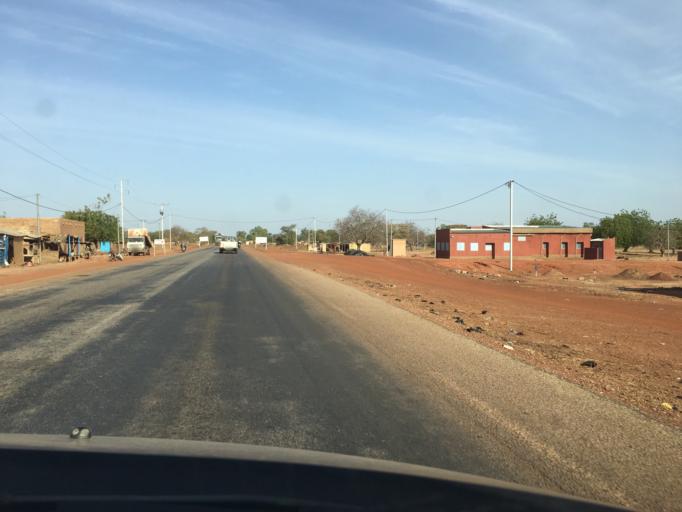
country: BF
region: Plateau-Central
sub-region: Province du Kourweogo
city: Bousse
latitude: 12.5332
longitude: -1.7800
